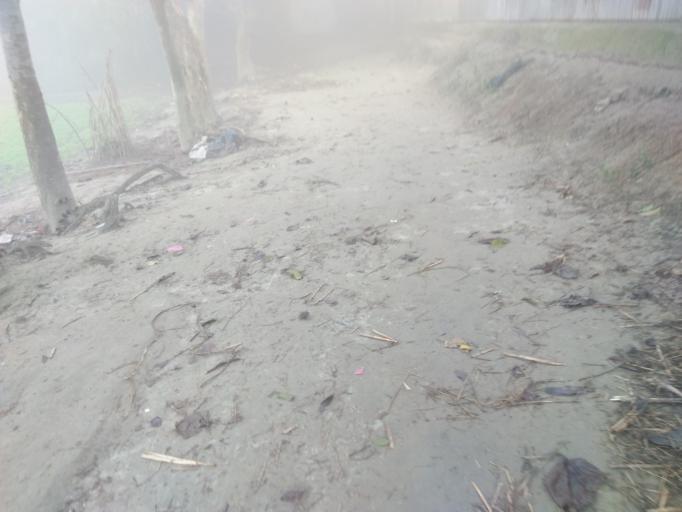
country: BD
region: Dhaka
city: Azimpur
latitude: 23.6879
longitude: 90.2987
